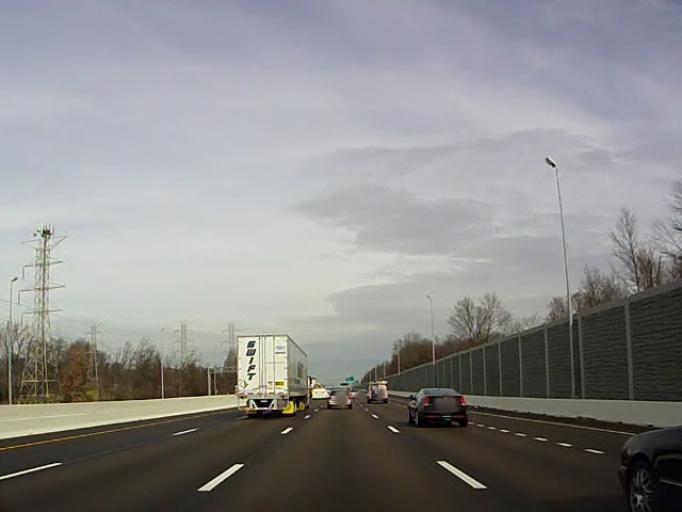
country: US
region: Tennessee
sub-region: Shelby County
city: Germantown
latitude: 35.1146
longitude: -89.8694
